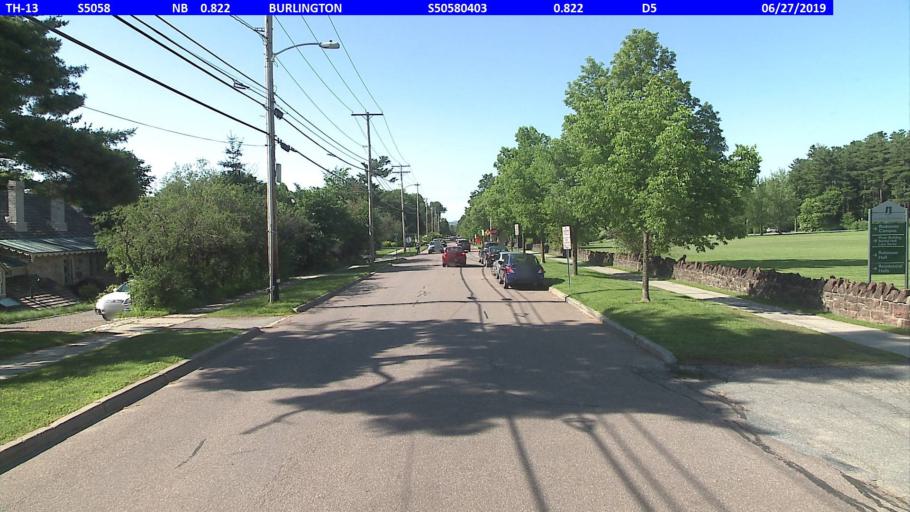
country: US
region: Vermont
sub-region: Chittenden County
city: Burlington
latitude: 44.4692
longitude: -73.2004
